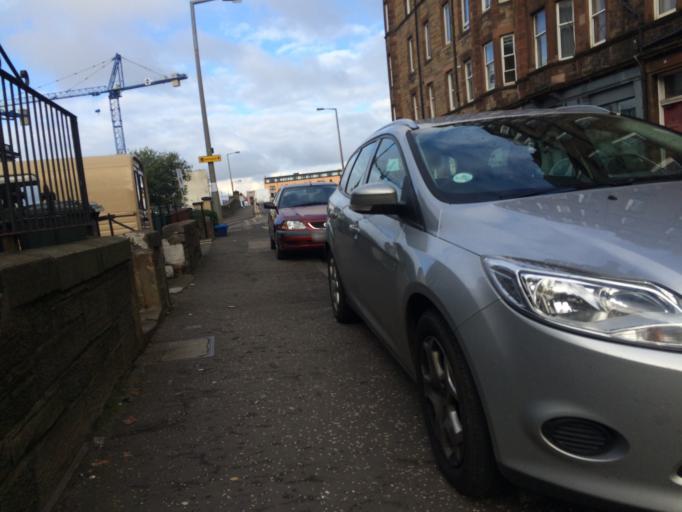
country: GB
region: Scotland
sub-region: Edinburgh
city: Edinburgh
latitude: 55.9401
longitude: -3.2126
